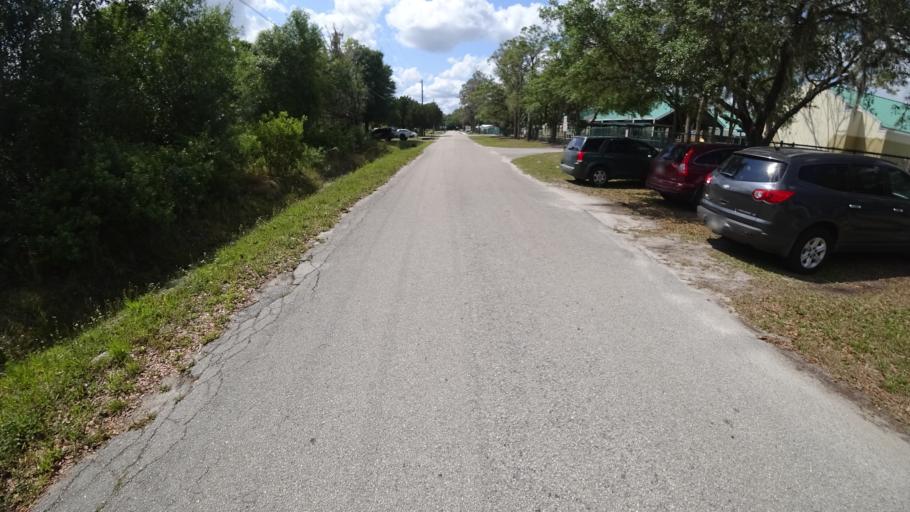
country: US
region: Florida
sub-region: Sarasota County
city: Lake Sarasota
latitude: 27.3518
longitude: -82.1605
